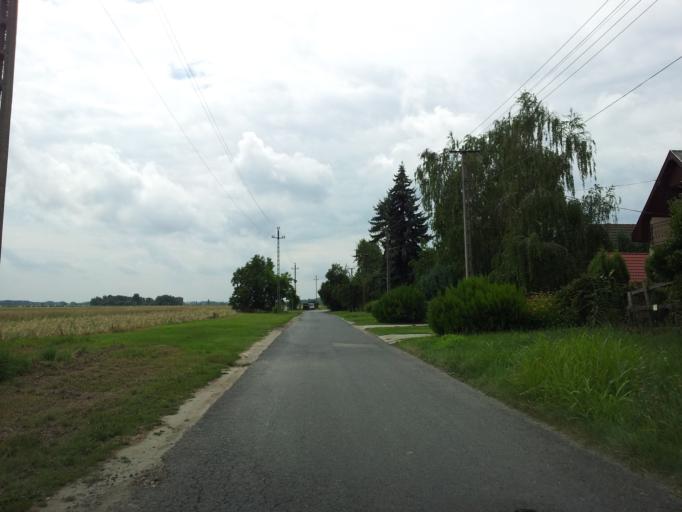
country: HU
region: Pest
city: Rackeve
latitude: 47.1907
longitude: 18.9598
